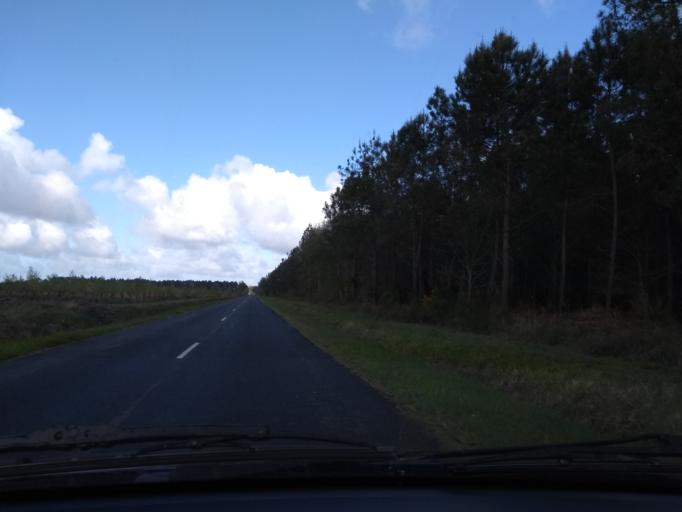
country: FR
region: Aquitaine
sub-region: Departement de la Gironde
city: Mios
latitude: 44.5503
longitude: -0.9682
